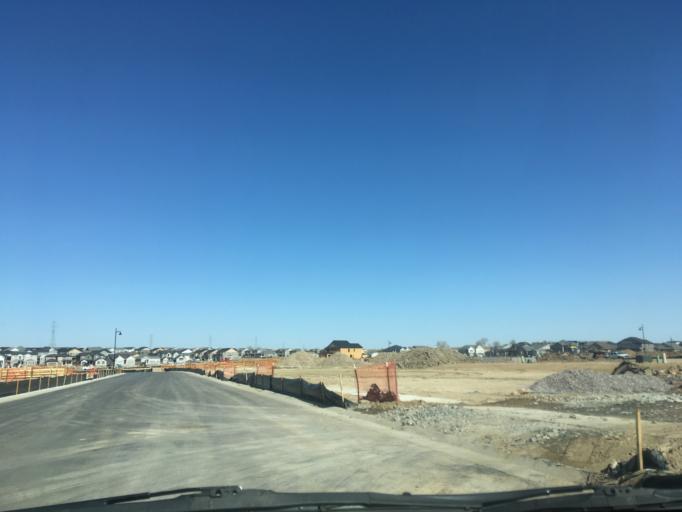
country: US
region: Colorado
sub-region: Boulder County
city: Erie
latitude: 40.0534
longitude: -105.0329
